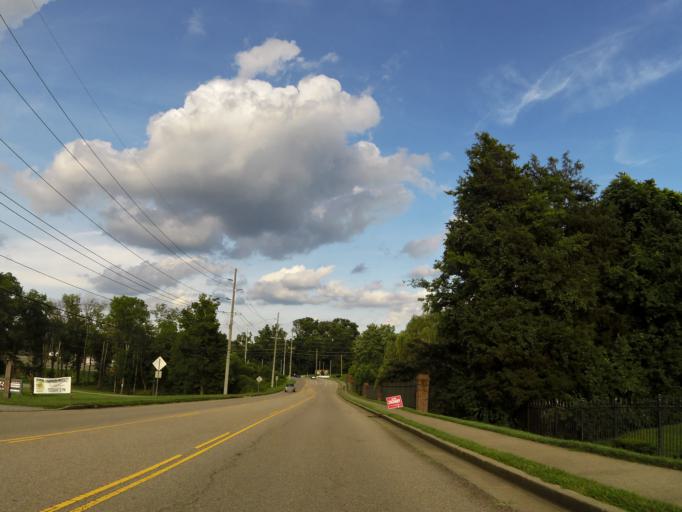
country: US
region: Tennessee
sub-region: Blount County
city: Louisville
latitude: 35.8913
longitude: -84.0706
